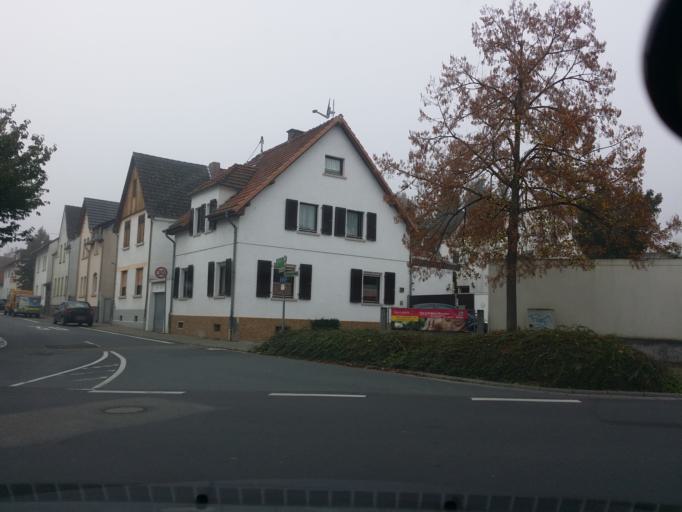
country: DE
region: Hesse
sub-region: Regierungsbezirk Darmstadt
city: Hofheim am Taunus
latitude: 50.0742
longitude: 8.4372
